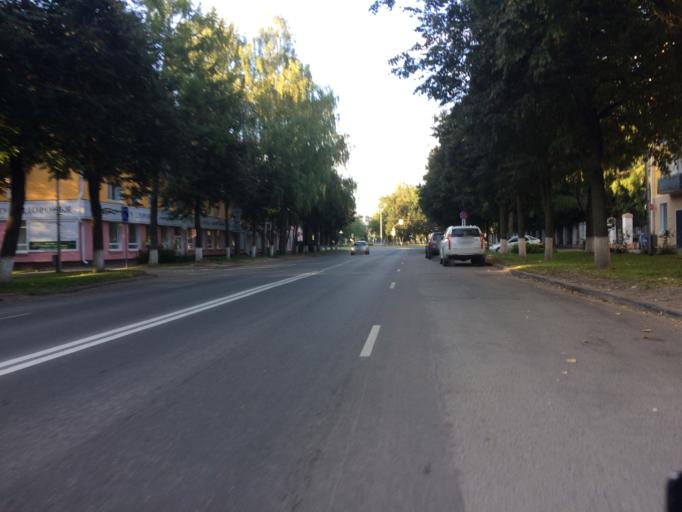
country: RU
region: Mariy-El
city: Yoshkar-Ola
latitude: 56.6267
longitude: 47.8862
